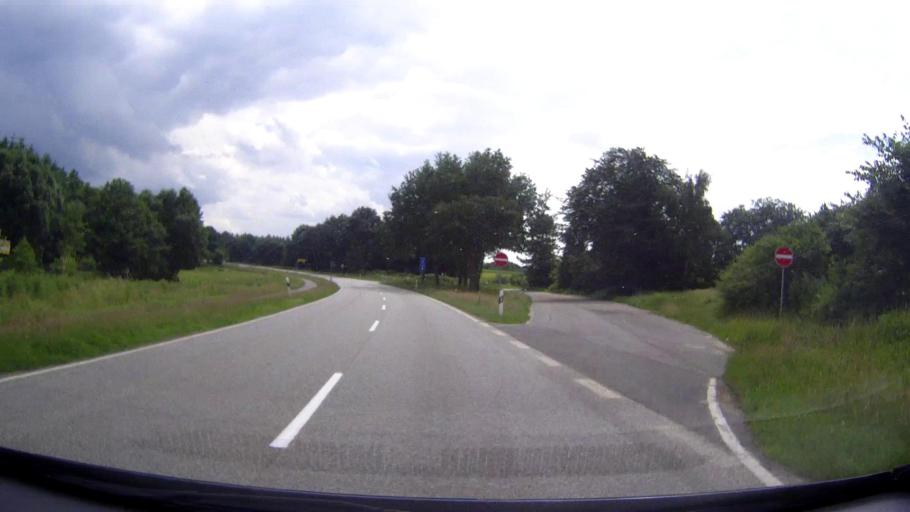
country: DE
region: Schleswig-Holstein
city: Warringholz
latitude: 54.0799
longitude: 9.4634
